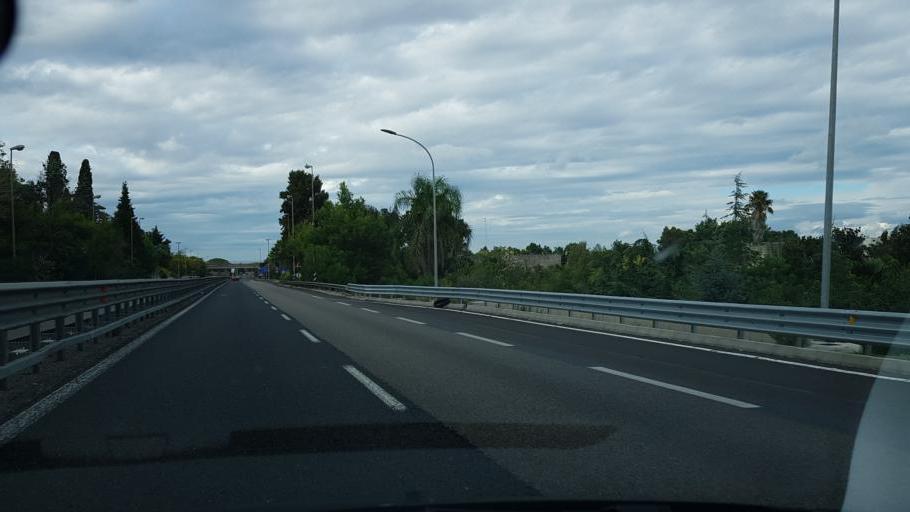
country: IT
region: Apulia
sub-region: Provincia di Lecce
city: Cavallino
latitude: 40.3050
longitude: 18.1915
